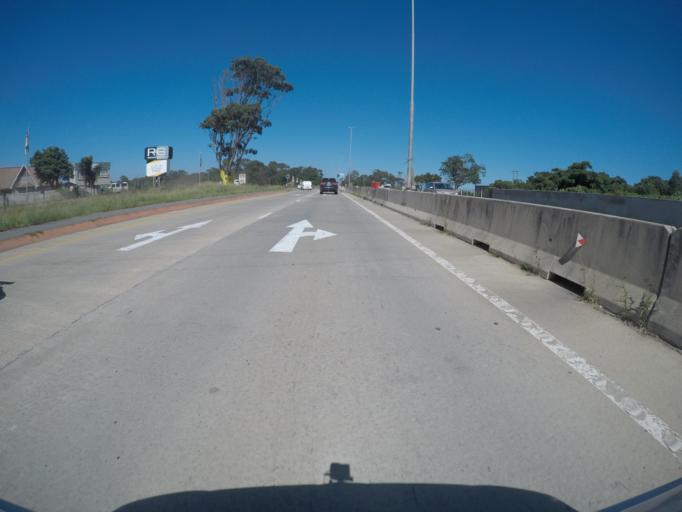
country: ZA
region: Eastern Cape
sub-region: Buffalo City Metropolitan Municipality
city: East London
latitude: -32.9371
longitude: 27.9837
